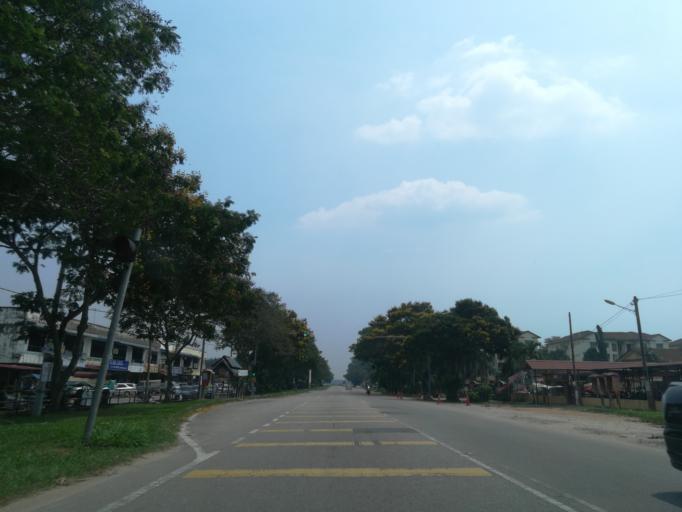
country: MY
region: Penang
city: Tasek Glugor
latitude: 5.4395
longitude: 100.5374
